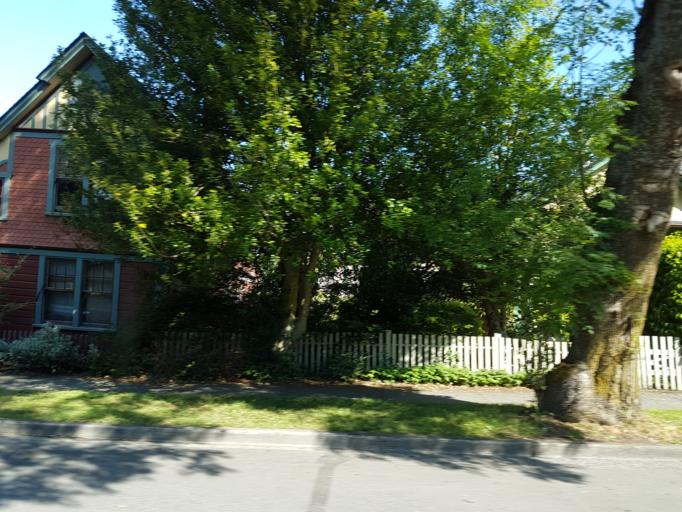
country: CA
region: British Columbia
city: Victoria
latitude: 48.4280
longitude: -123.3397
